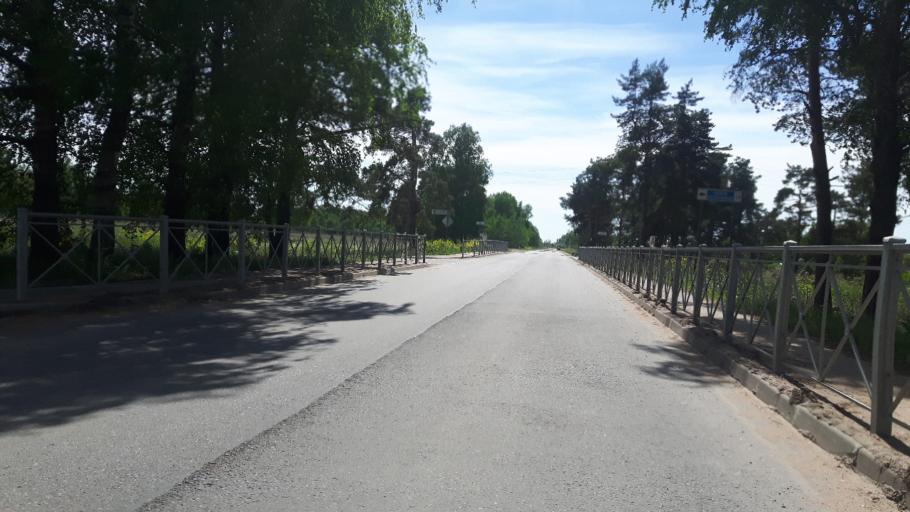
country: RU
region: Leningrad
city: Ust'-Luga
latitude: 59.5783
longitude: 28.1762
